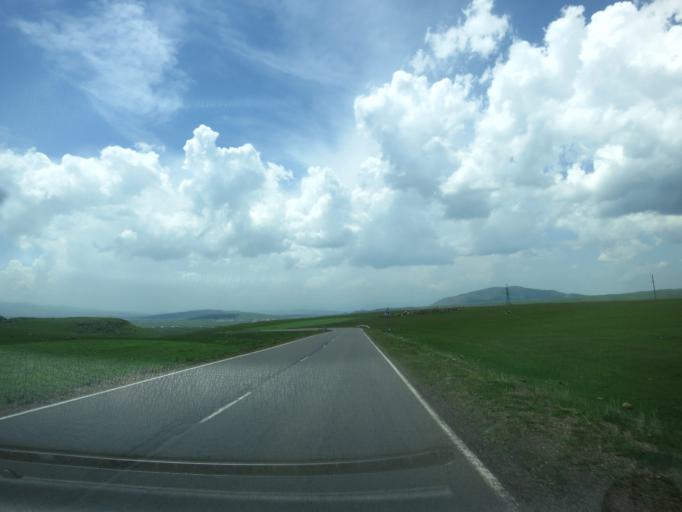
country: GE
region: Samtskhe-Javakheti
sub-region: Ninotsminda
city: Ninotsminda
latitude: 41.2952
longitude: 43.6827
